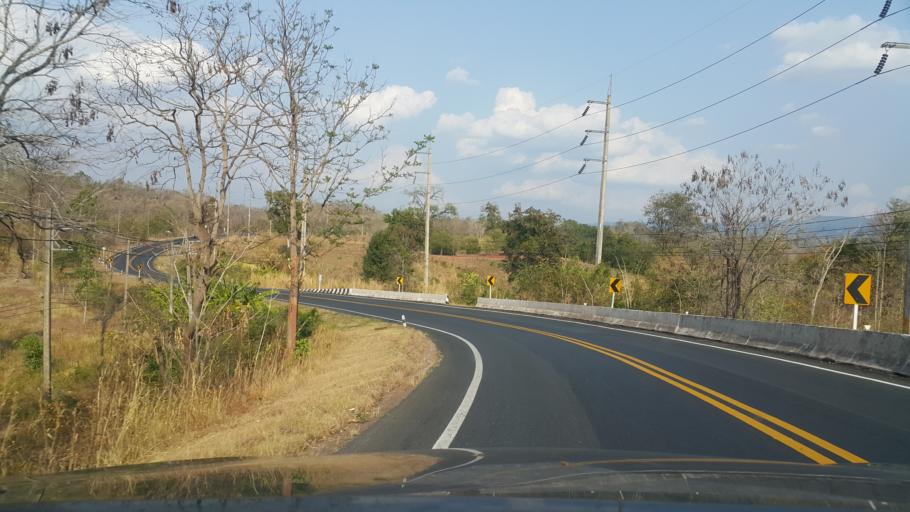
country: TH
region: Phitsanulok
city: Nakhon Thai
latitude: 17.1773
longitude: 100.9945
